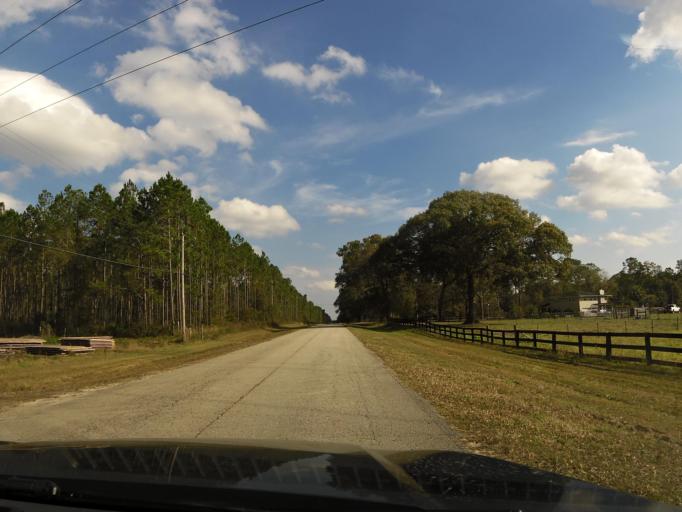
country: US
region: Florida
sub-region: Duval County
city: Baldwin
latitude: 30.1577
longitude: -81.9921
